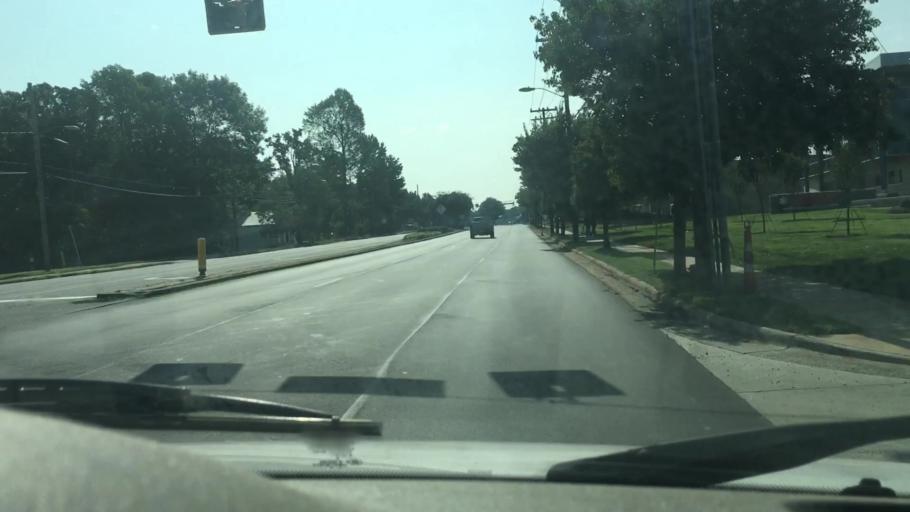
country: US
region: North Carolina
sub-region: Mecklenburg County
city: Charlotte
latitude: 35.2272
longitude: -80.9125
